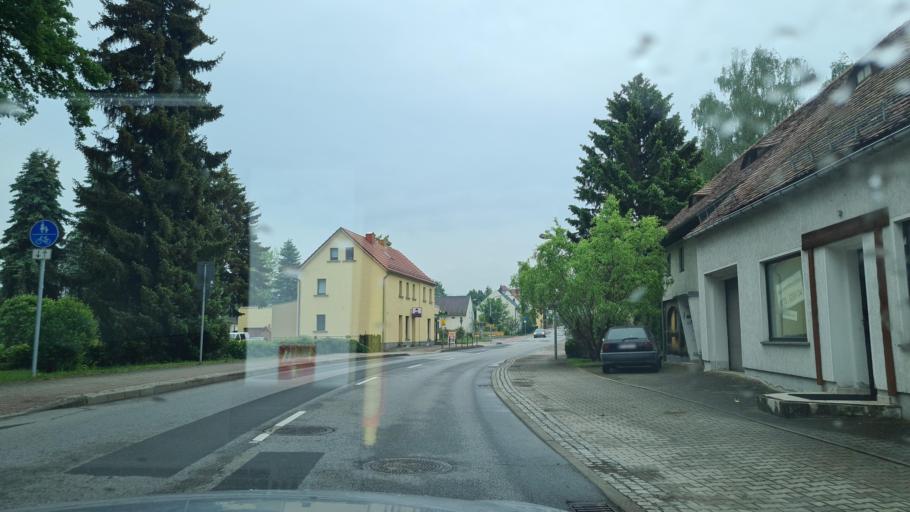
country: DE
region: Saxony
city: Grosspostwitz
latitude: 51.1045
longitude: 14.4457
